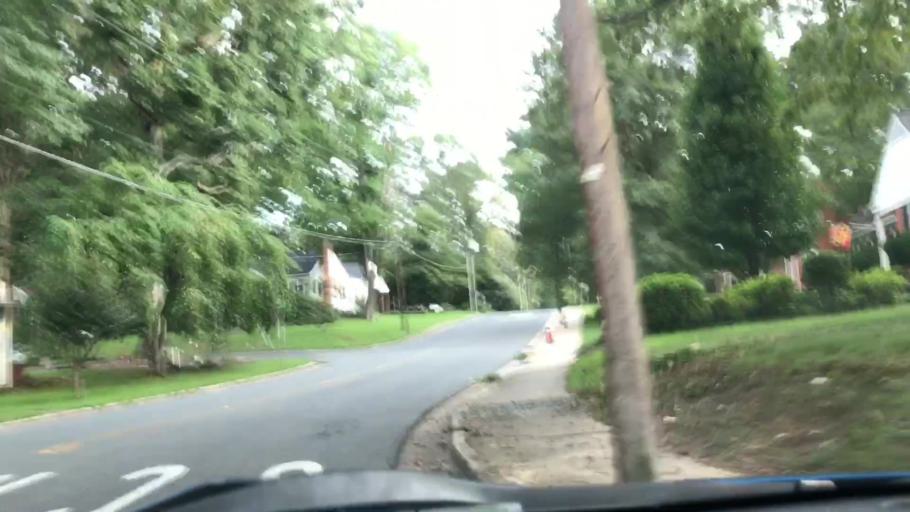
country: US
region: North Carolina
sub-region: Randolph County
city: Asheboro
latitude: 35.7021
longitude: -79.8061
